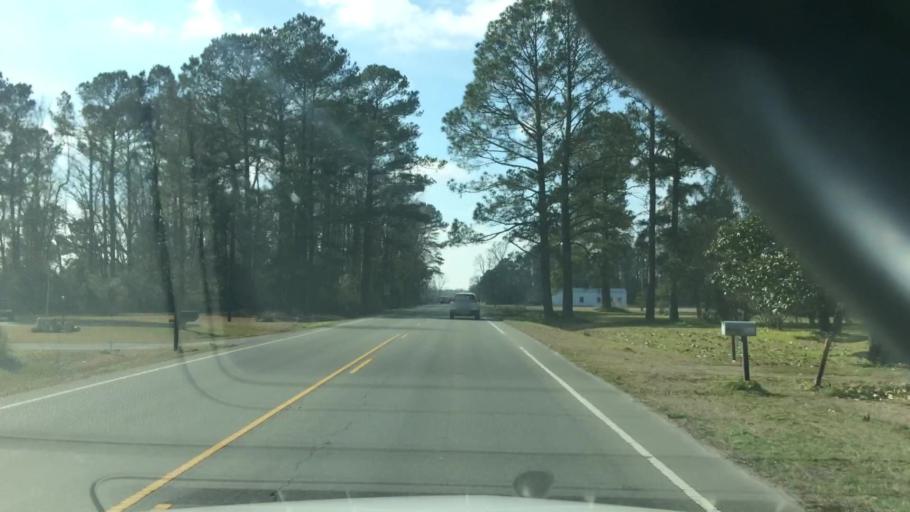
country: US
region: North Carolina
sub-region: Duplin County
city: Beulaville
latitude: 34.8326
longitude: -77.8035
